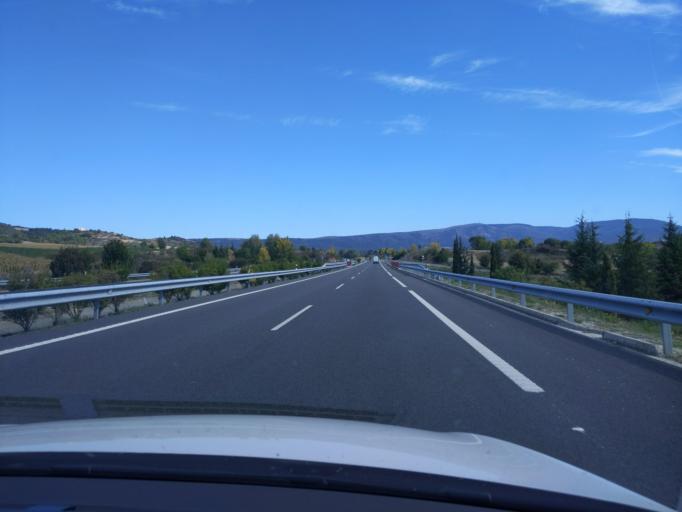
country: ES
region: Navarre
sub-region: Provincia de Navarra
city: Obanos
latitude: 42.6949
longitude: -1.7921
